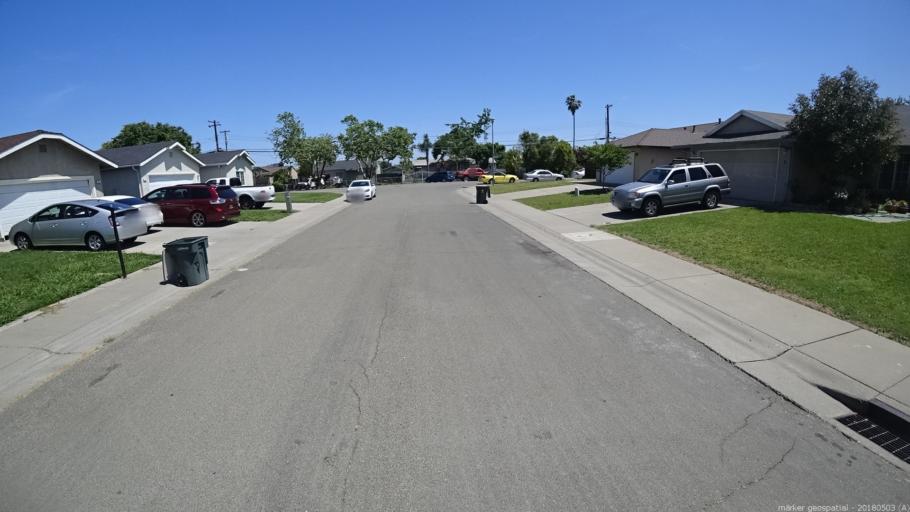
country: US
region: California
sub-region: Sacramento County
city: Arden-Arcade
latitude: 38.6423
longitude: -121.4159
